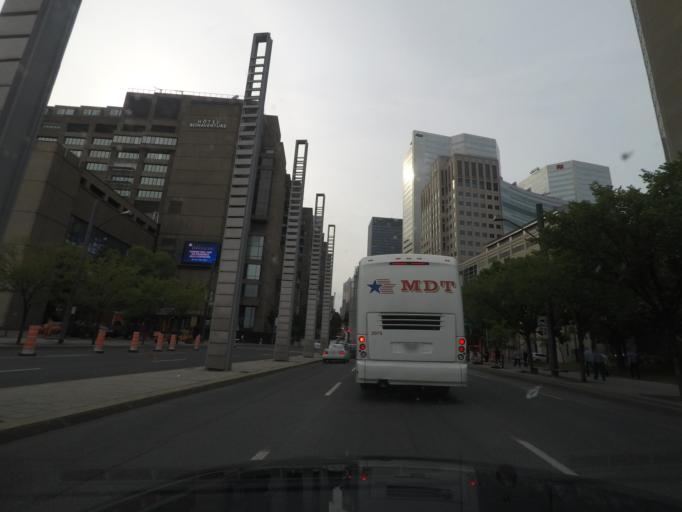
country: CA
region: Quebec
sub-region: Montreal
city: Montreal
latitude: 45.4993
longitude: -73.5628
